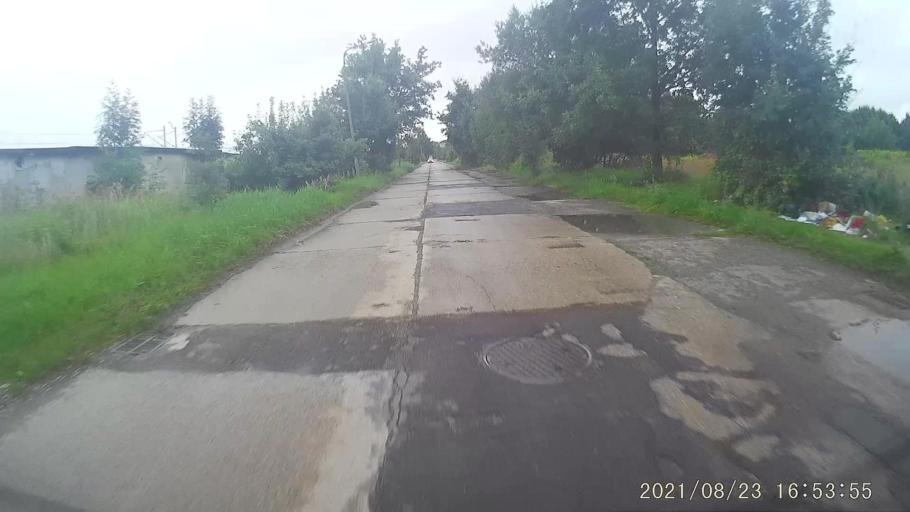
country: PL
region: Lower Silesian Voivodeship
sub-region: Powiat zgorzelecki
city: Zgorzelec
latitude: 51.1618
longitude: 15.0187
